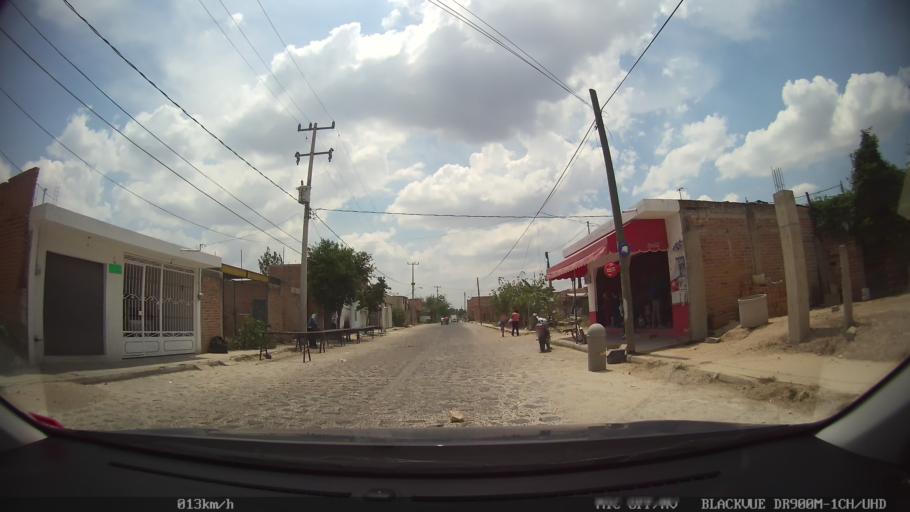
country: MX
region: Jalisco
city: Tonala
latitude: 20.6786
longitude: -103.2376
